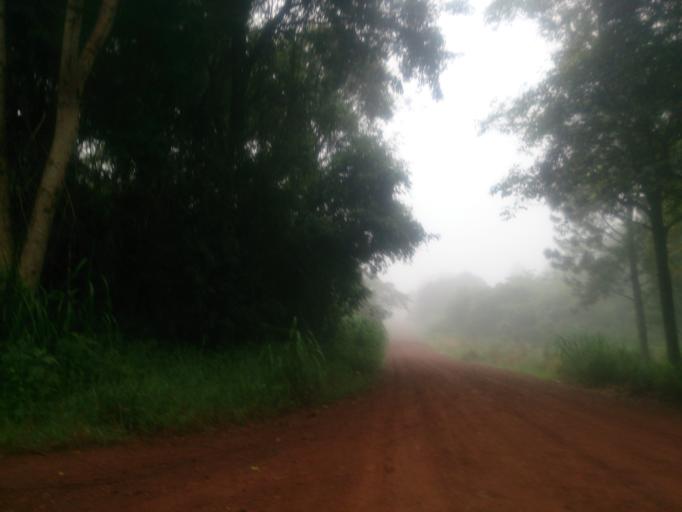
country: AR
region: Misiones
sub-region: Departamento de Obera
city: Obera
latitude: -27.4672
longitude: -55.1062
